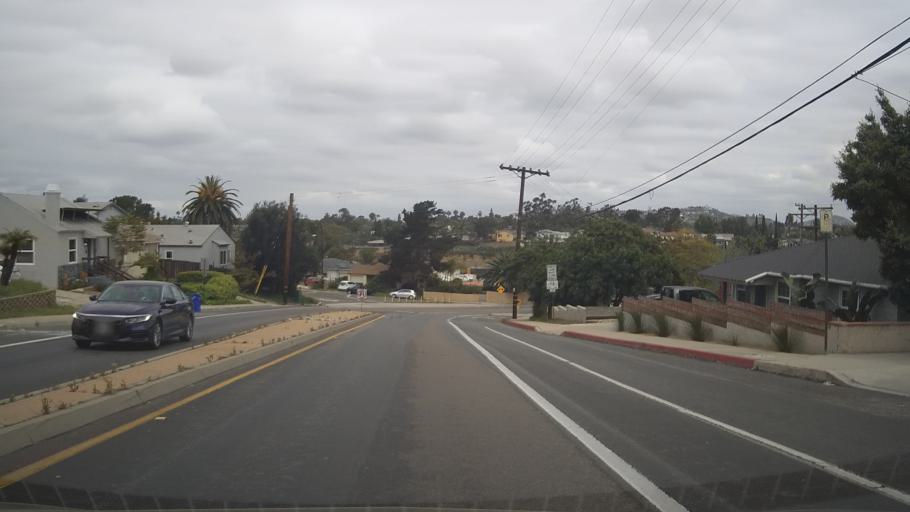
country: US
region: California
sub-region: San Diego County
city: Lemon Grove
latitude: 32.7526
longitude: -117.0430
